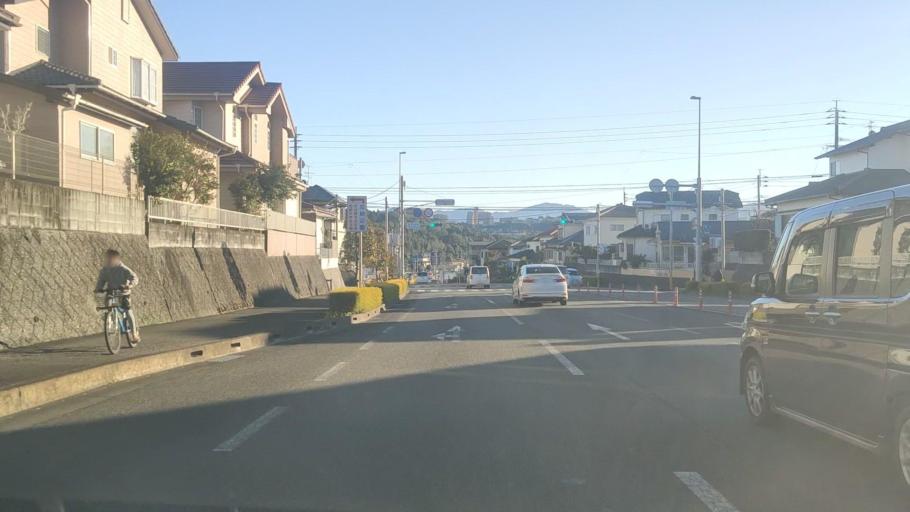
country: JP
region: Miyazaki
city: Miyazaki-shi
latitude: 31.8749
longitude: 131.3921
